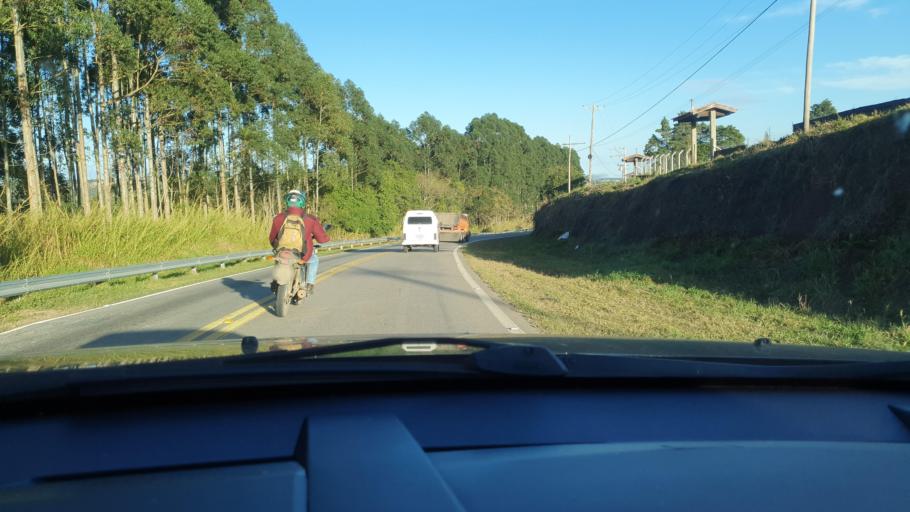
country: BR
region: Sao Paulo
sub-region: Piedade
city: Piedade
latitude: -23.7162
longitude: -47.3797
